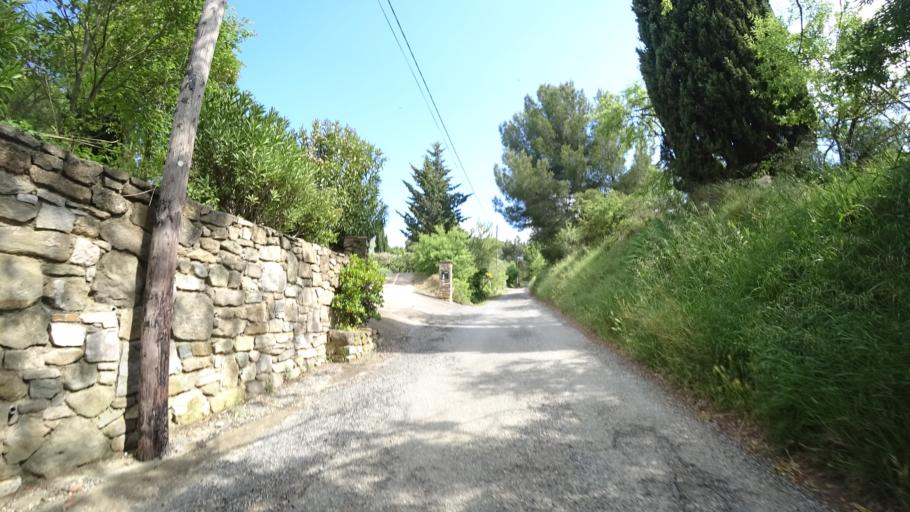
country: FR
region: Languedoc-Roussillon
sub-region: Departement de l'Aude
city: Ginestas
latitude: 43.2649
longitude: 2.8737
